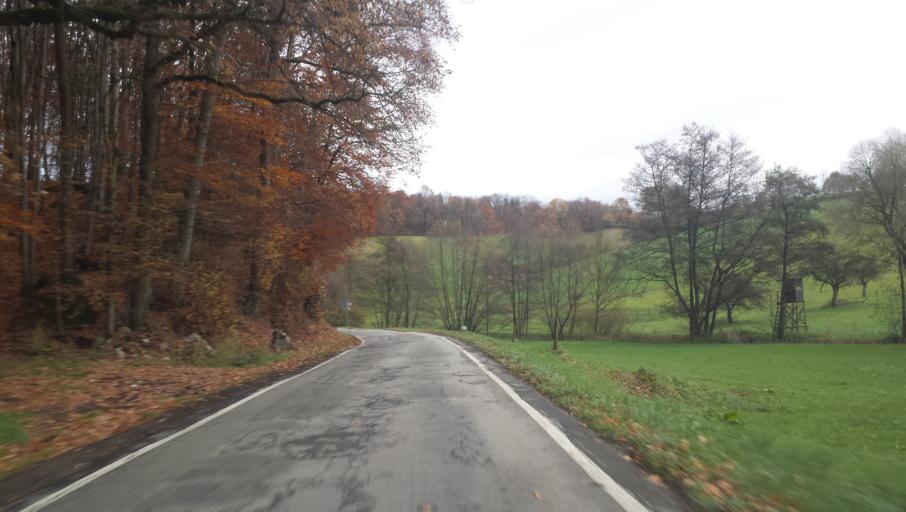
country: DE
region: Hesse
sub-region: Regierungsbezirk Darmstadt
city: Morlenbach
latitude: 49.5945
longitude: 8.7059
